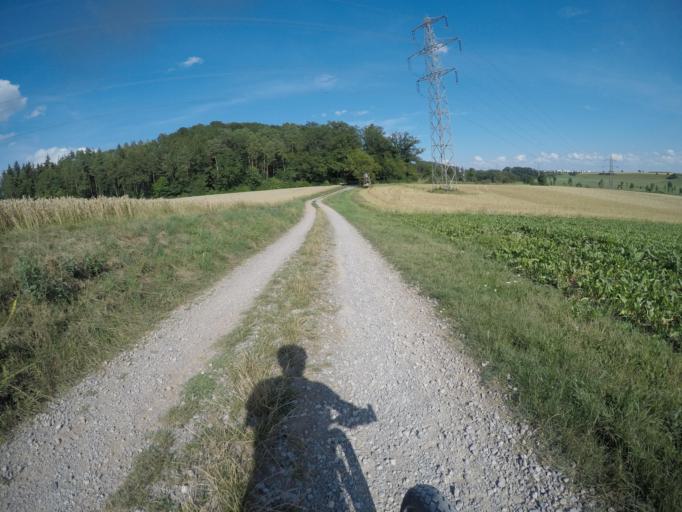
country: DE
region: Baden-Wuerttemberg
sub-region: Regierungsbezirk Stuttgart
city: Altdorf
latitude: 48.6522
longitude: 8.9843
